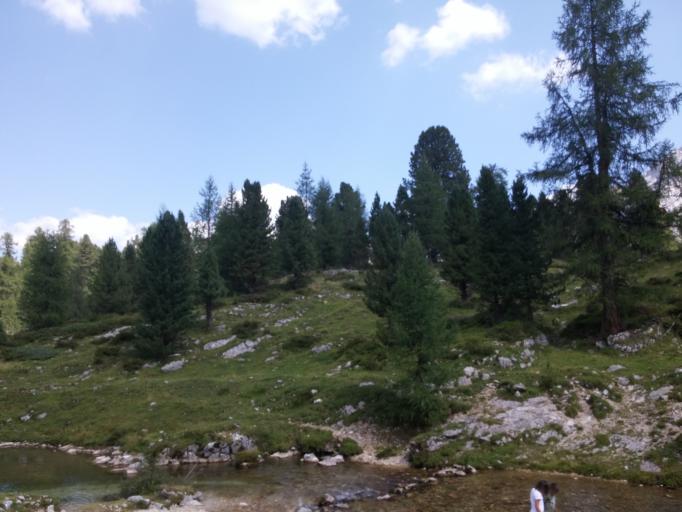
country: IT
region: Trentino-Alto Adige
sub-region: Bolzano
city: San Genesio
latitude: 46.6165
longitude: 12.0137
